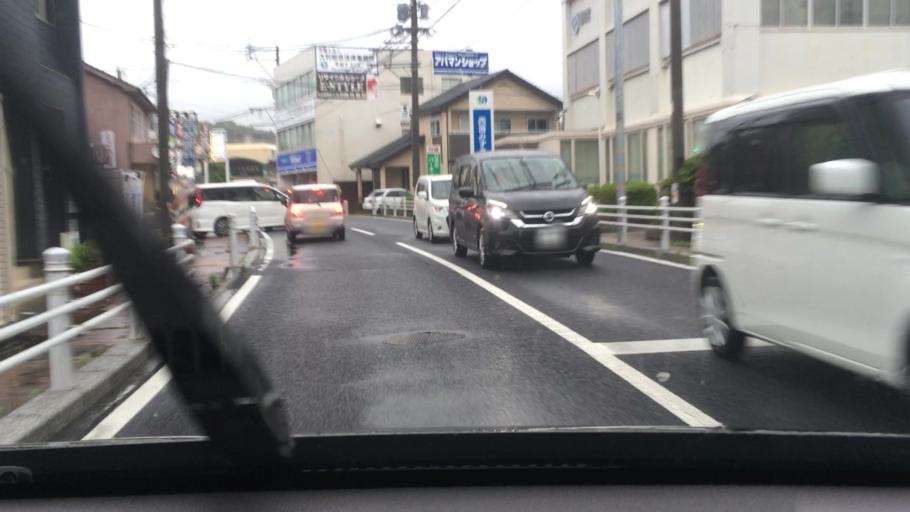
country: JP
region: Nagasaki
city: Sasebo
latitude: 33.1358
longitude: 129.7985
